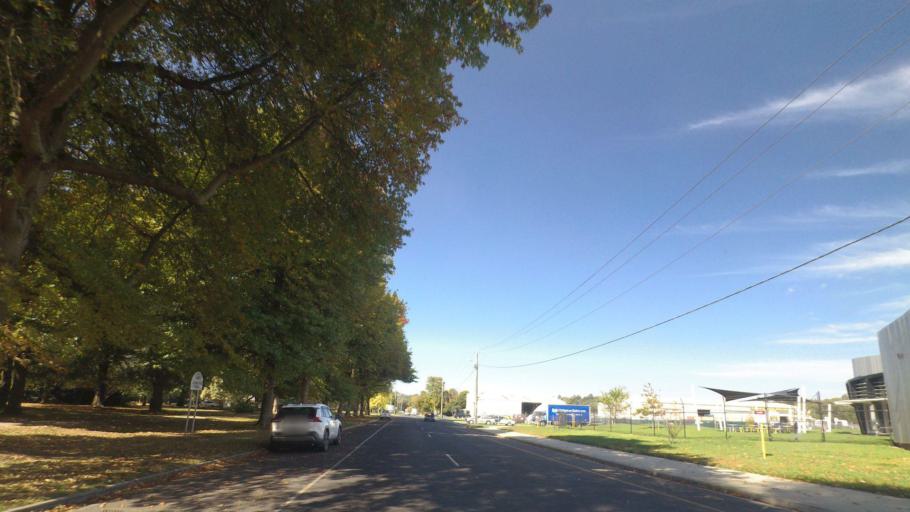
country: AU
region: Victoria
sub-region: Baw Baw
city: Warragul
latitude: -38.1667
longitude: 145.9280
